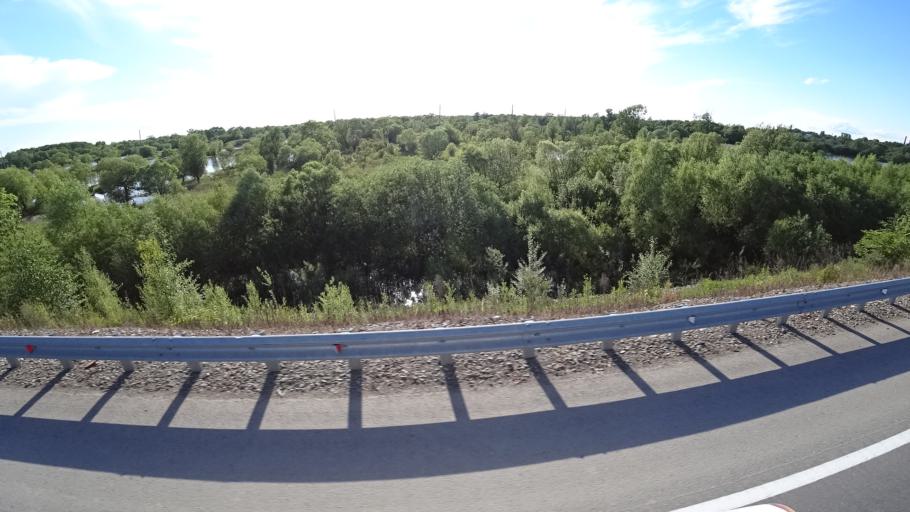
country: RU
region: Khabarovsk Krai
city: Khor
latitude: 47.8617
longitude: 134.9632
